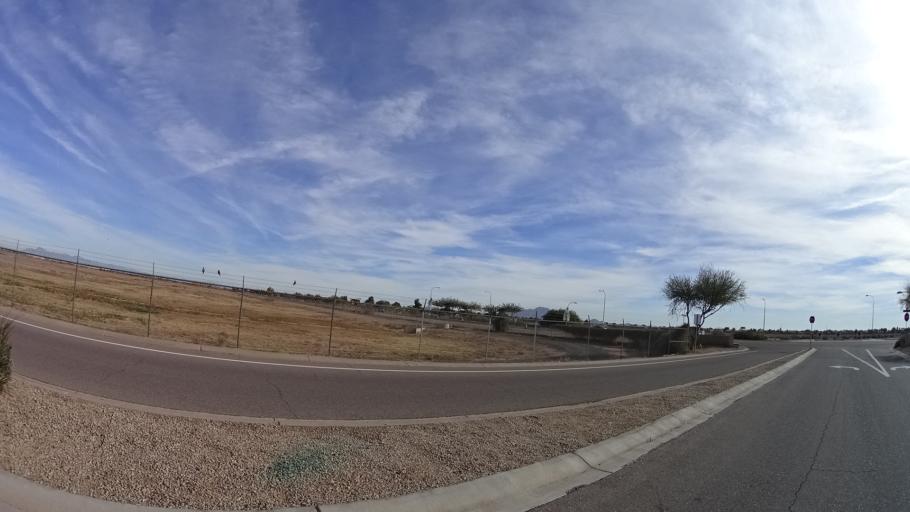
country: US
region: Arizona
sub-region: Maricopa County
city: Chandler
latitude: 33.2631
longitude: -111.8217
